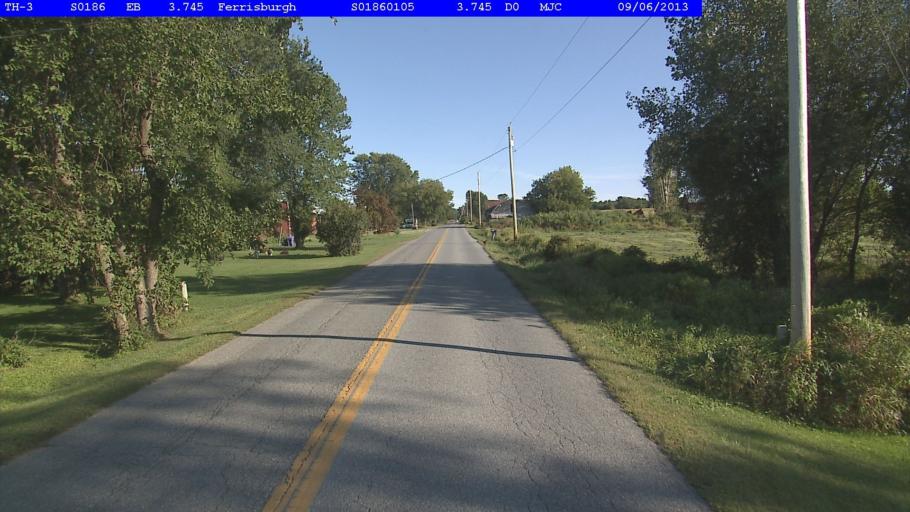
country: US
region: Vermont
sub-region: Addison County
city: Vergennes
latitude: 44.1735
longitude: -73.3044
